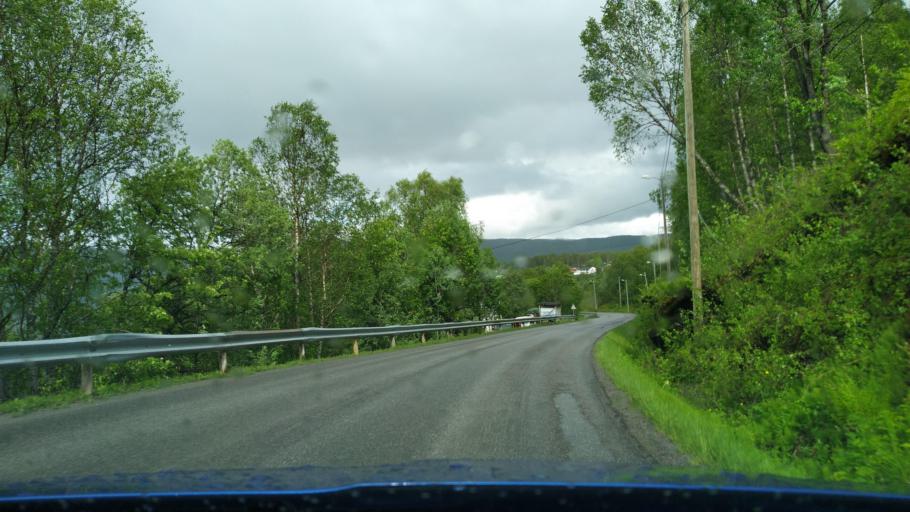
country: NO
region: Troms
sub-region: Sorreisa
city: Sorreisa
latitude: 69.1393
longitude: 18.1019
